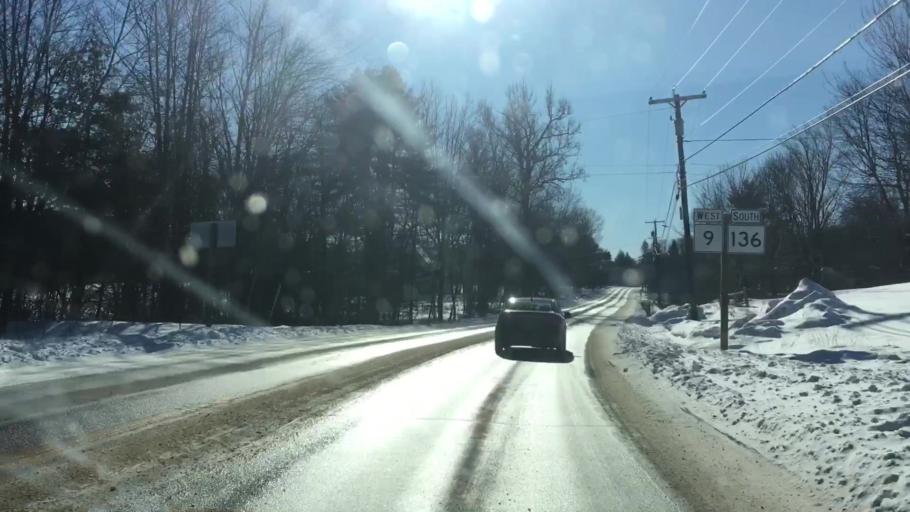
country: US
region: Maine
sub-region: Androscoggin County
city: Lisbon
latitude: 43.9801
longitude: -70.1250
